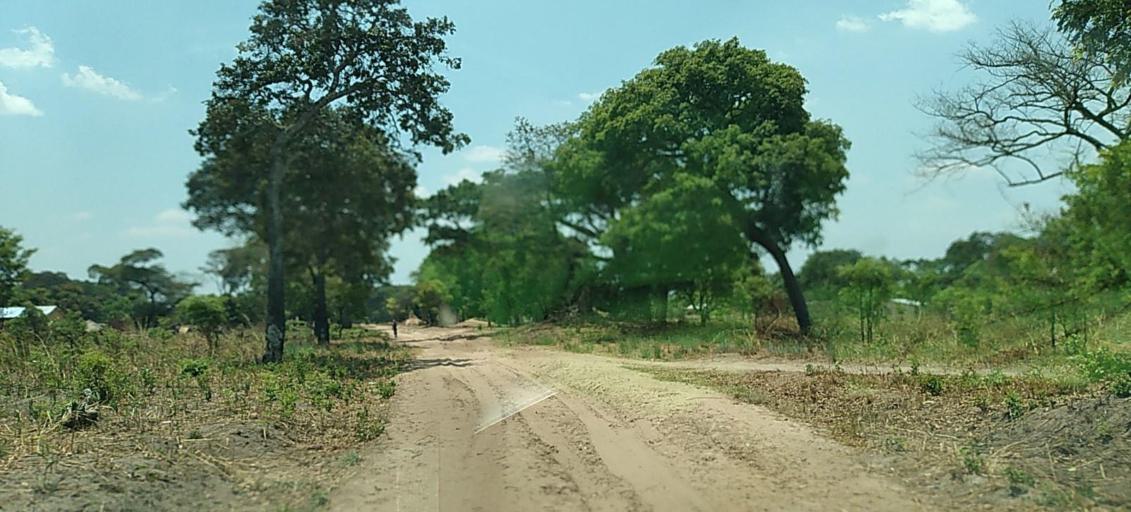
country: CD
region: Katanga
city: Kolwezi
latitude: -11.3740
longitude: 25.2153
